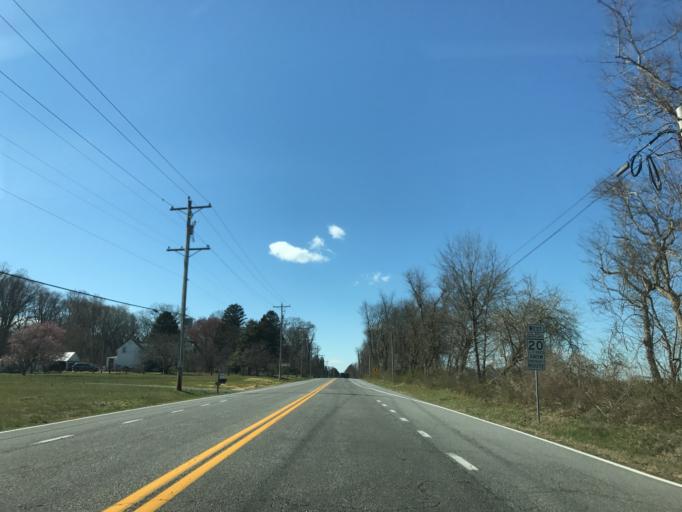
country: US
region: Maryland
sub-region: Kent County
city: Chestertown
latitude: 39.2148
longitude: -76.1140
